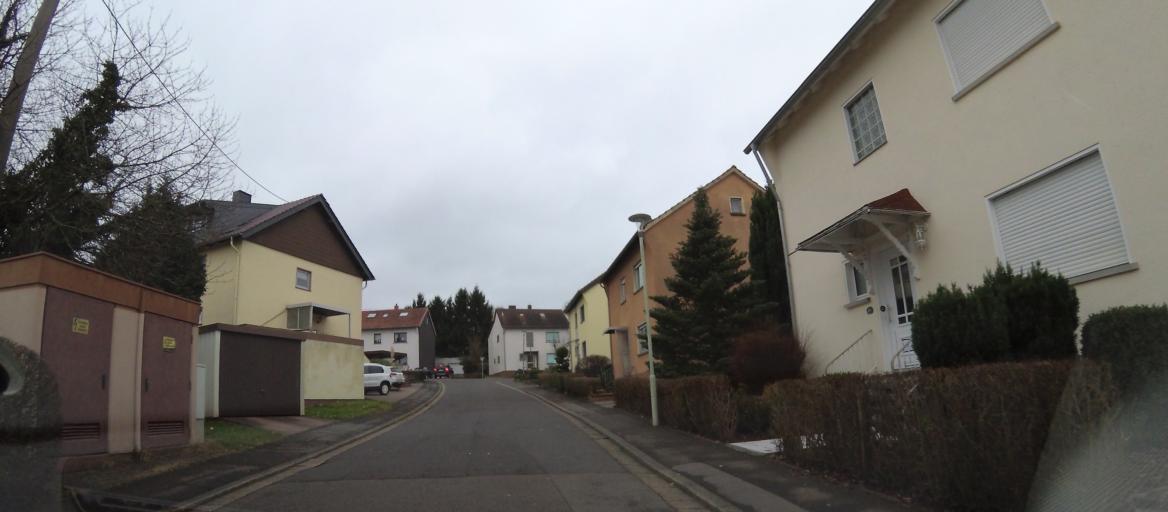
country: DE
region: Saarland
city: Schiffweiler
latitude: 49.3592
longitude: 7.1163
